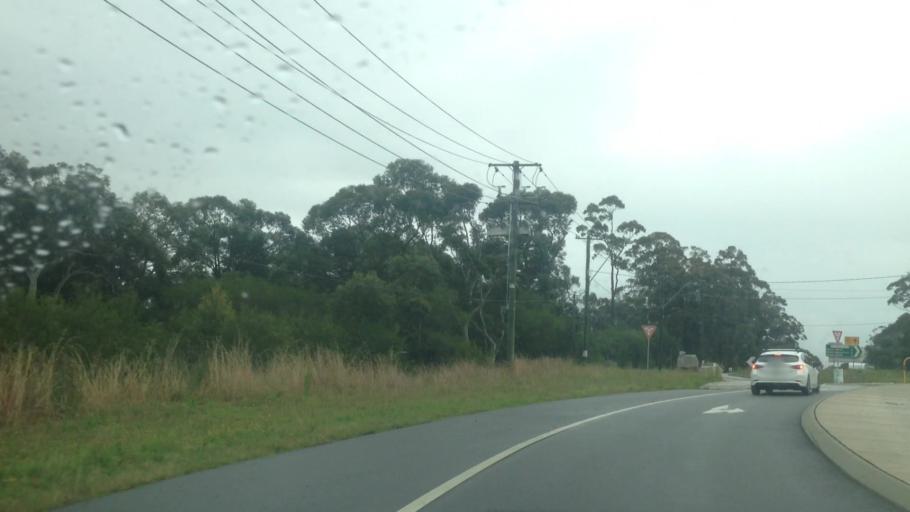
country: AU
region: New South Wales
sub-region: Wyong Shire
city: Charmhaven
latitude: -33.1570
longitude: 151.4787
